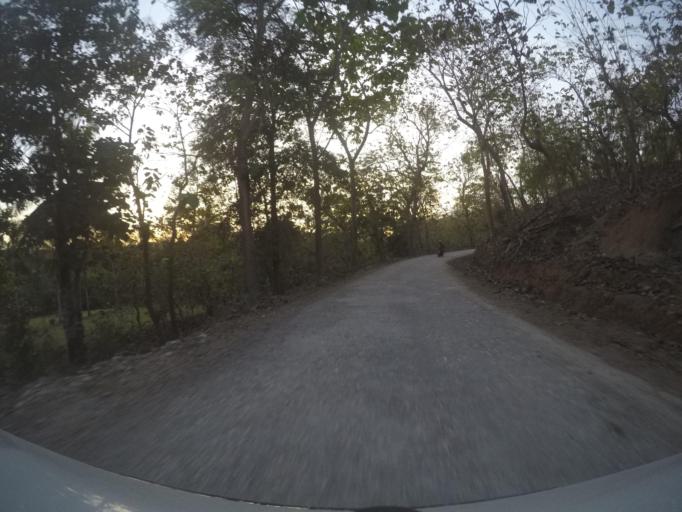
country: TL
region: Viqueque
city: Viqueque
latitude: -8.8963
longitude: 126.3893
